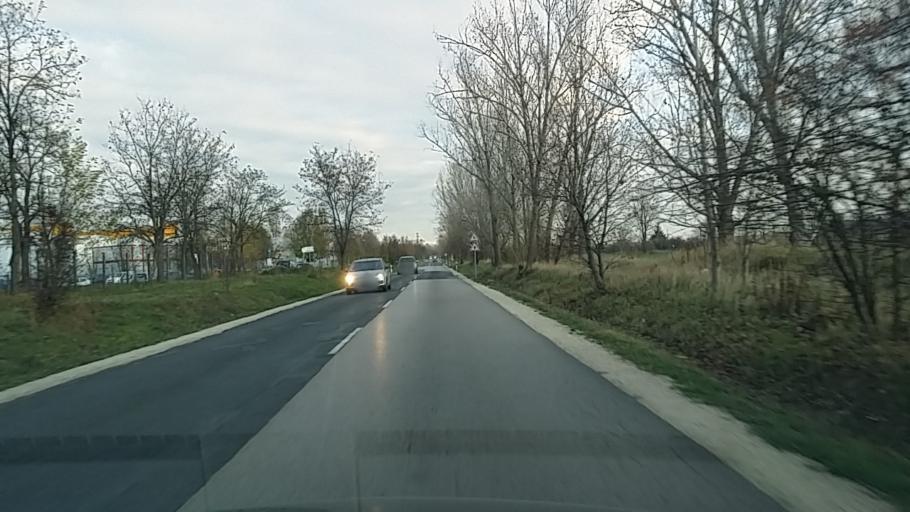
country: HU
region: Pest
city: Vac
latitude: 47.7710
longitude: 19.1641
